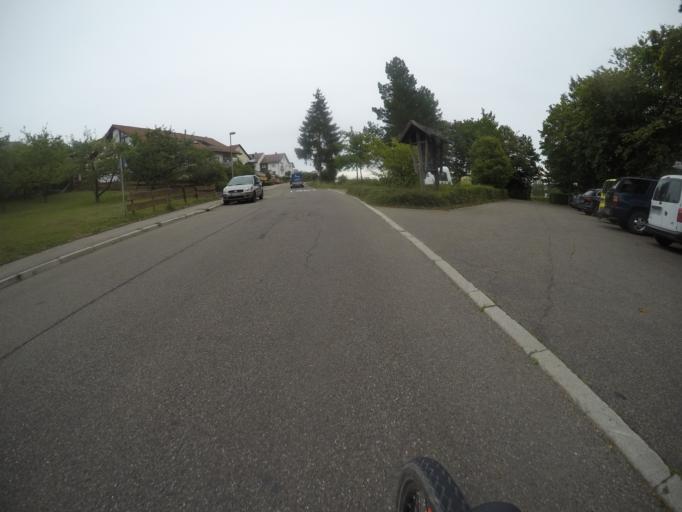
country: DE
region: Baden-Wuerttemberg
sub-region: Karlsruhe Region
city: Simmozheim
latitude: 48.7754
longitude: 8.8195
